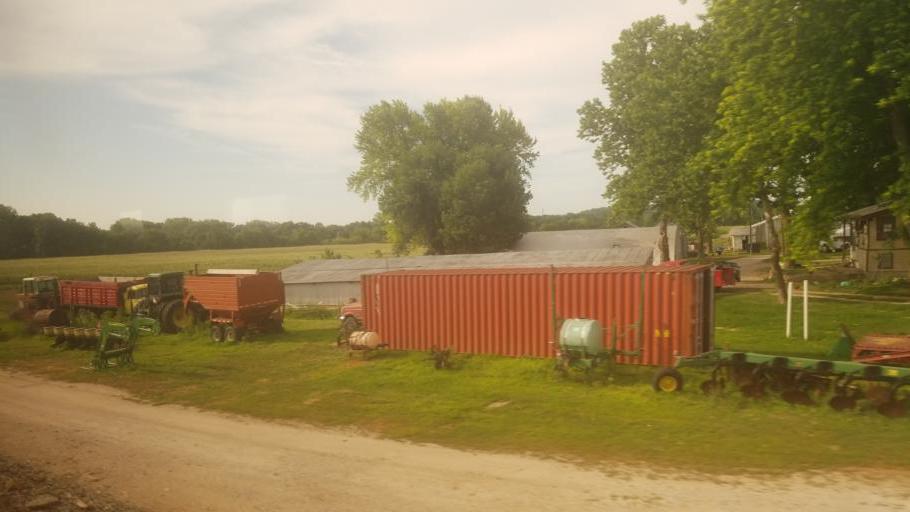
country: US
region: Kansas
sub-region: Douglas County
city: Lawrence
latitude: 39.0179
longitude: -95.2931
